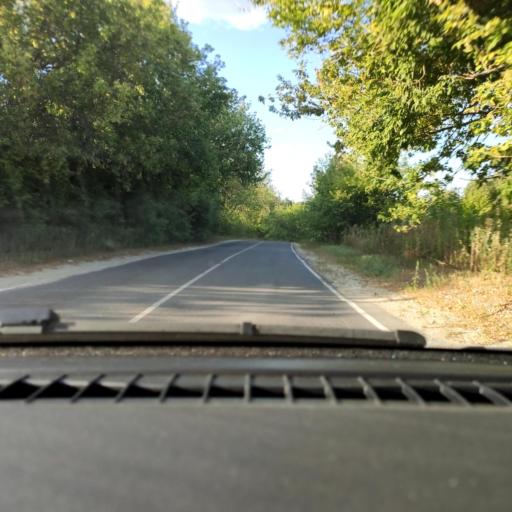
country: RU
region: Voronezj
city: Semiluki
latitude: 51.6626
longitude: 39.0111
